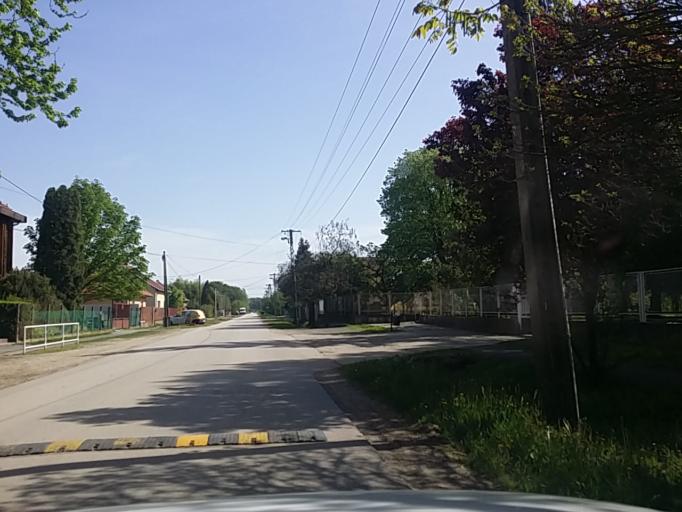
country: HU
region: Bekes
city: Doboz
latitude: 46.7003
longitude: 21.1861
